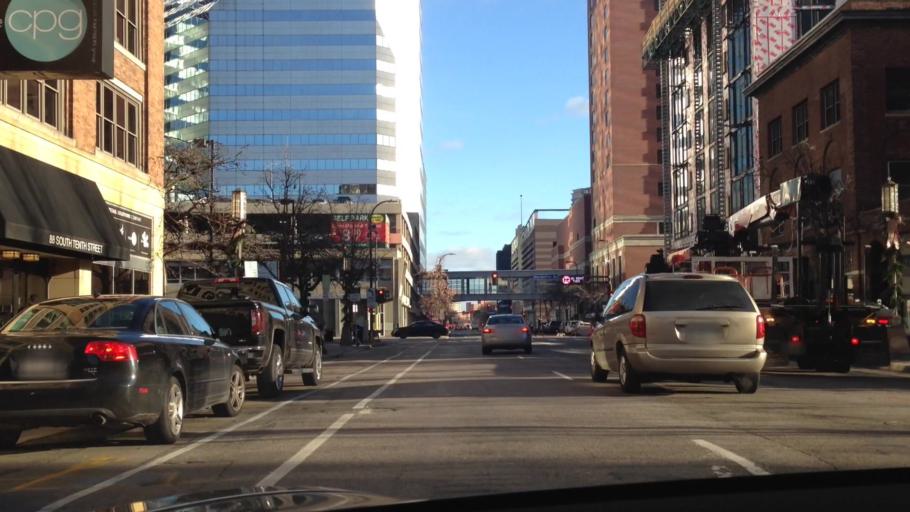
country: US
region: Minnesota
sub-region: Hennepin County
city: Minneapolis
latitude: 44.9738
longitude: -93.2743
